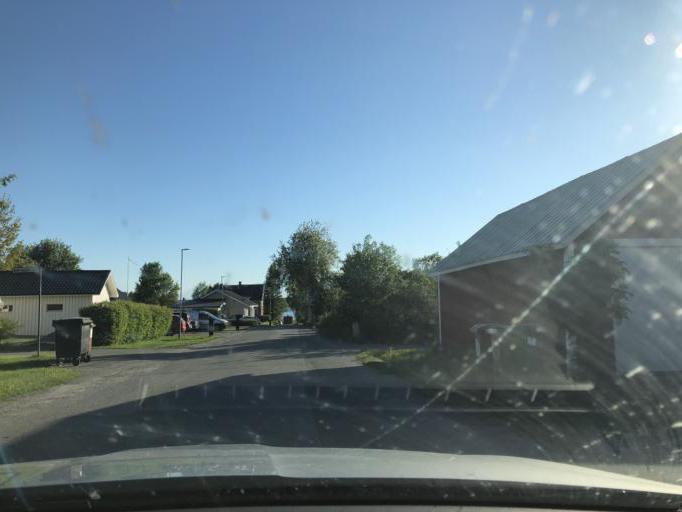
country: SE
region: Norrbotten
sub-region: Lulea Kommun
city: Sodra Sunderbyn
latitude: 65.6582
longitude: 21.9363
